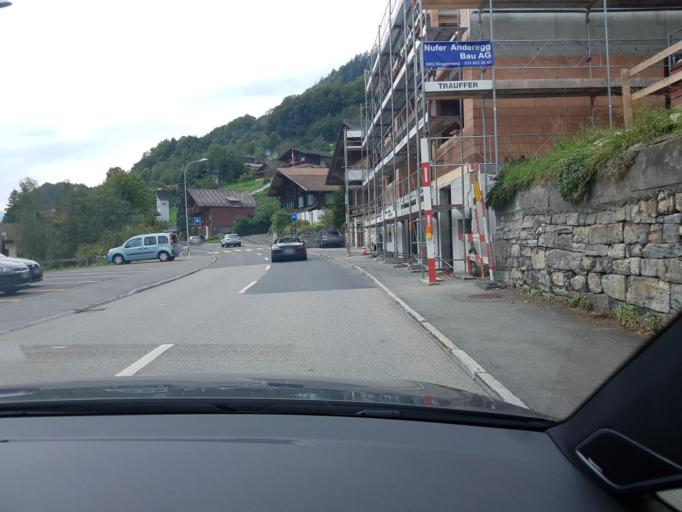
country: CH
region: Bern
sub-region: Interlaken-Oberhasli District
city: Ringgenberg
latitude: 46.7186
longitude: 7.9314
